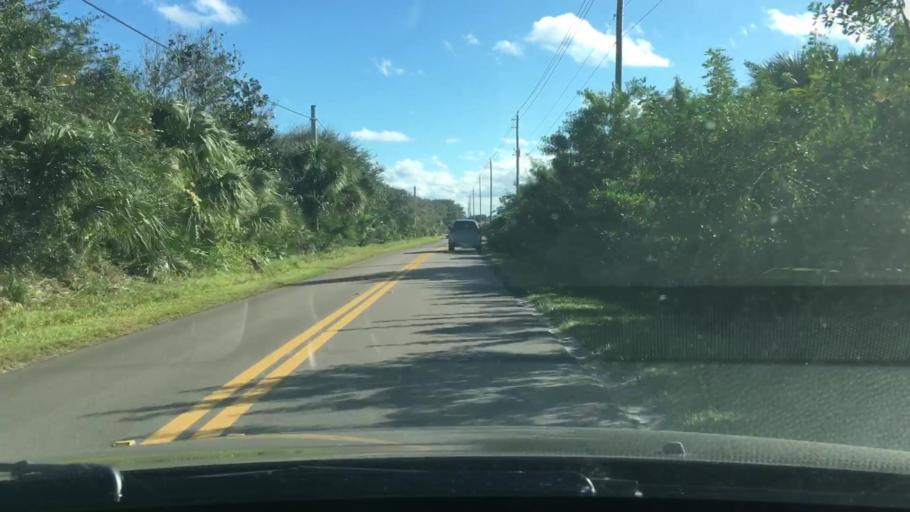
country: US
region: Florida
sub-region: Volusia County
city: Ormond-by-the-Sea
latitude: 29.4068
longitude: -81.0970
